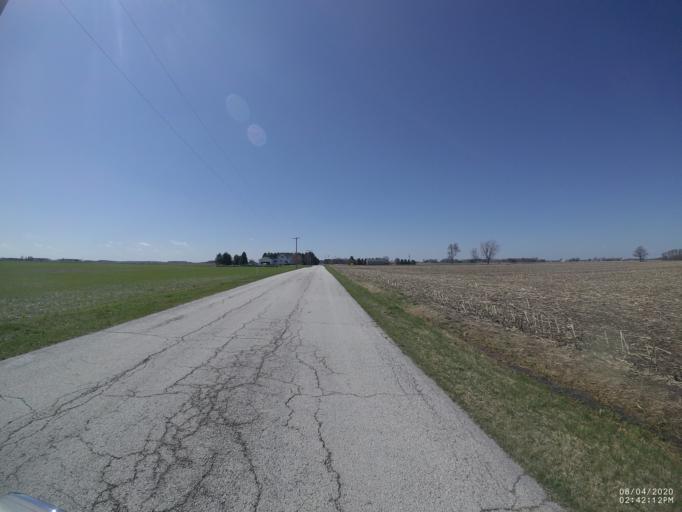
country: US
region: Ohio
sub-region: Sandusky County
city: Gibsonburg
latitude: 41.2902
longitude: -83.2977
